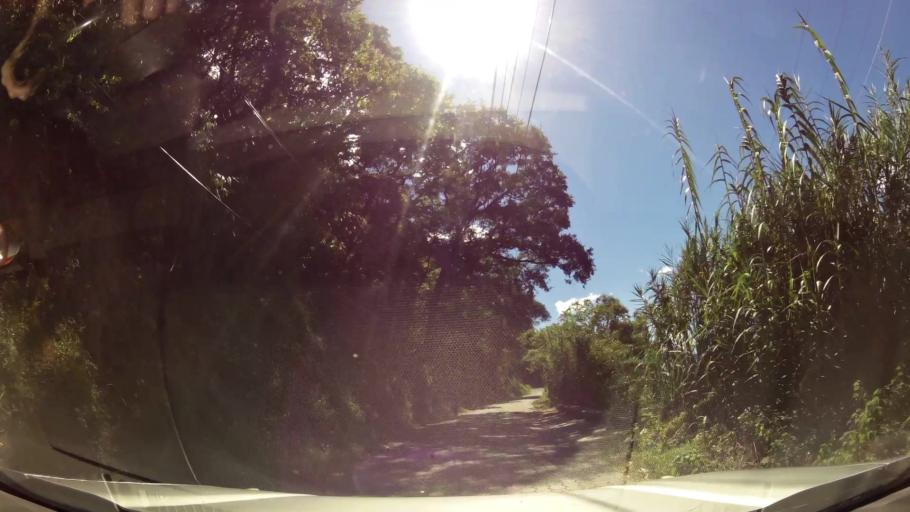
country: GT
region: Solola
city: Panajachel
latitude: 14.7455
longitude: -91.1630
